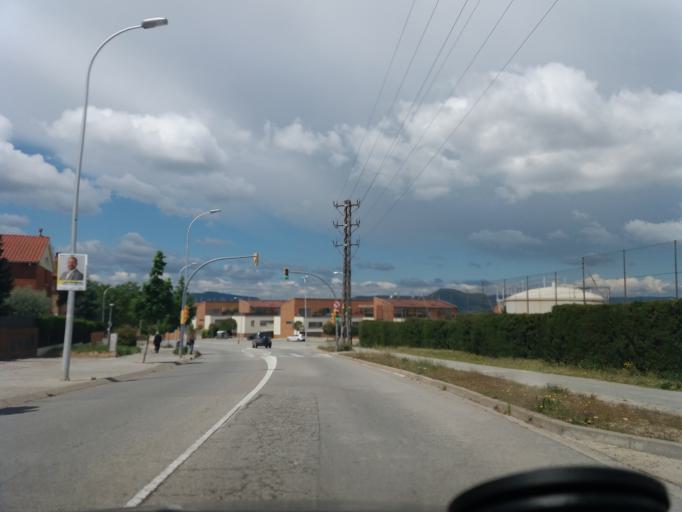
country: ES
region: Catalonia
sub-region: Provincia de Barcelona
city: Manresa
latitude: 41.7217
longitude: 1.8440
